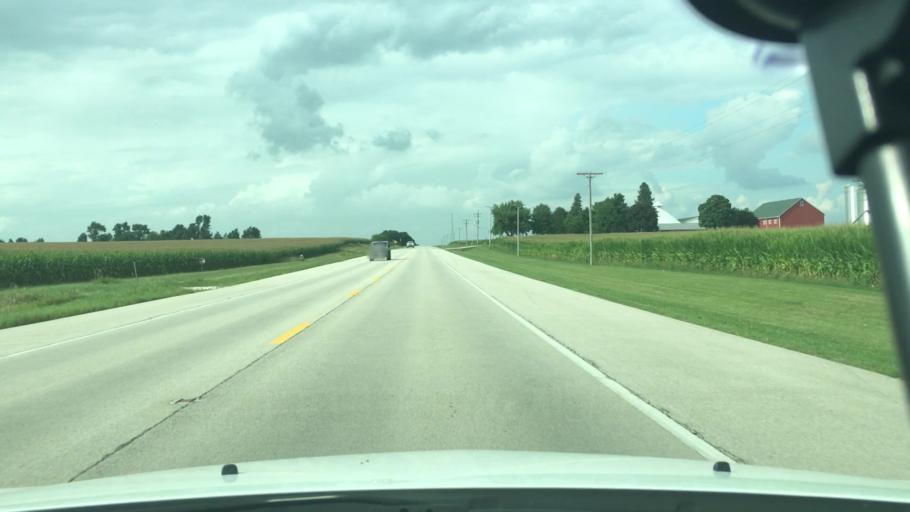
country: US
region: Illinois
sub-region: DeKalb County
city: Waterman
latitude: 41.7782
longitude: -88.7542
